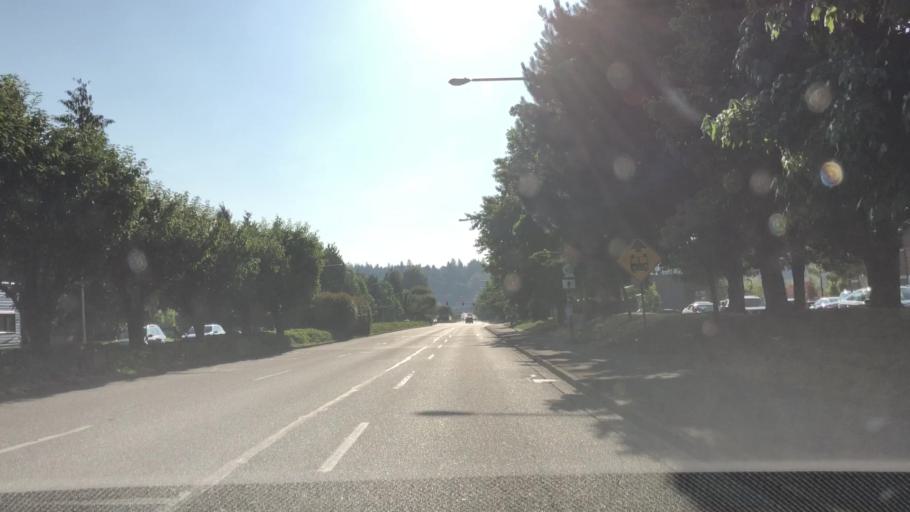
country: US
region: Washington
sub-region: King County
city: Auburn
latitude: 47.2959
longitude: -122.2418
